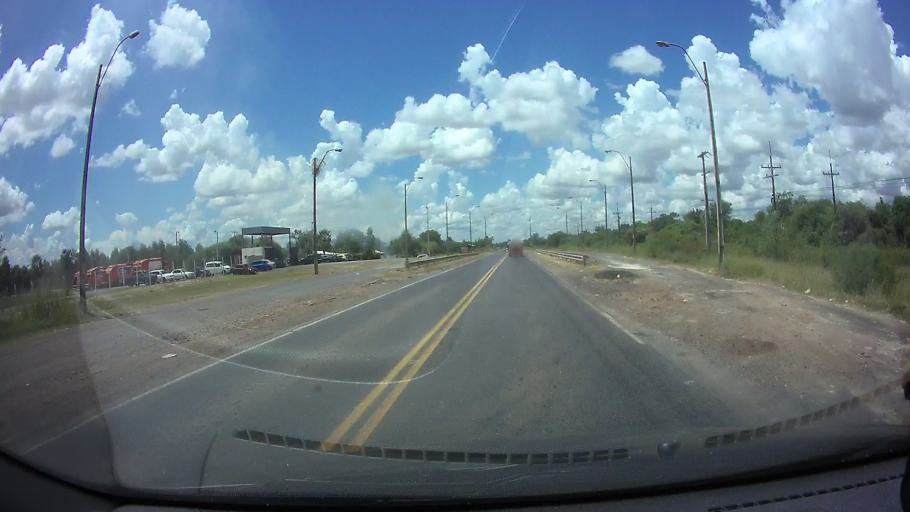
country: PY
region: Central
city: Colonia Mariano Roque Alonso
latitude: -25.1757
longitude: -57.5776
